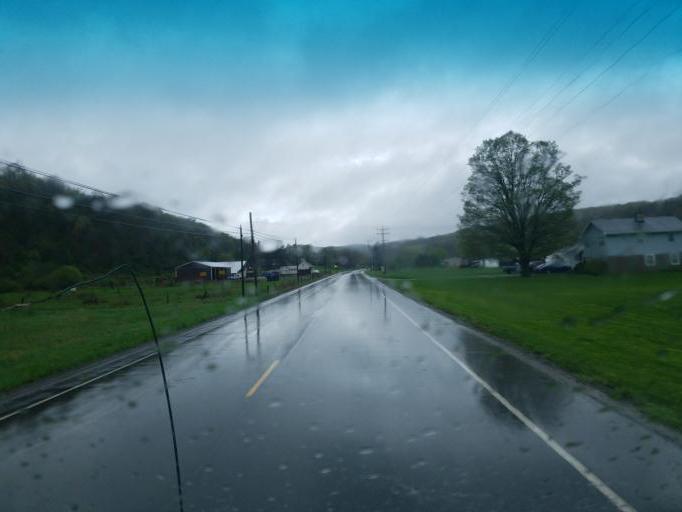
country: US
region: Pennsylvania
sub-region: Tioga County
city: Westfield
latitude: 41.9248
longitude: -77.6262
